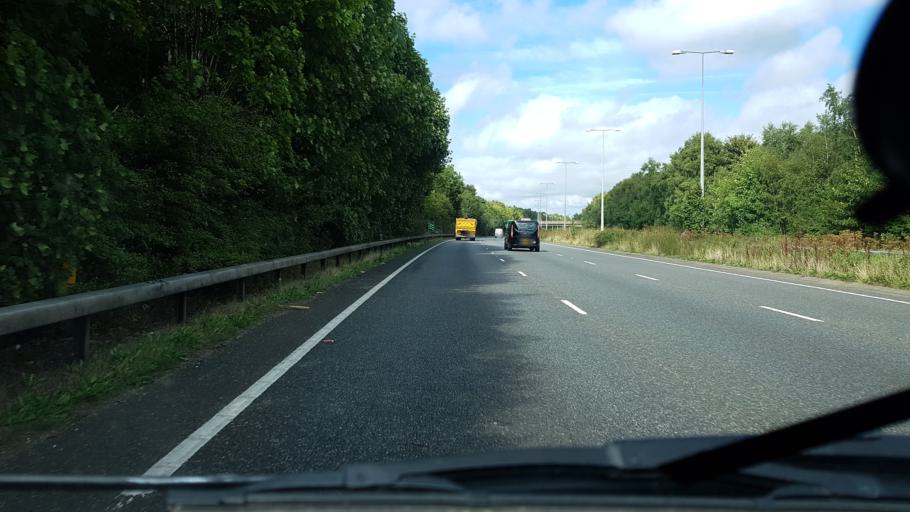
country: GB
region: England
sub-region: West Sussex
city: Broadfield
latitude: 51.0799
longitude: -0.2033
